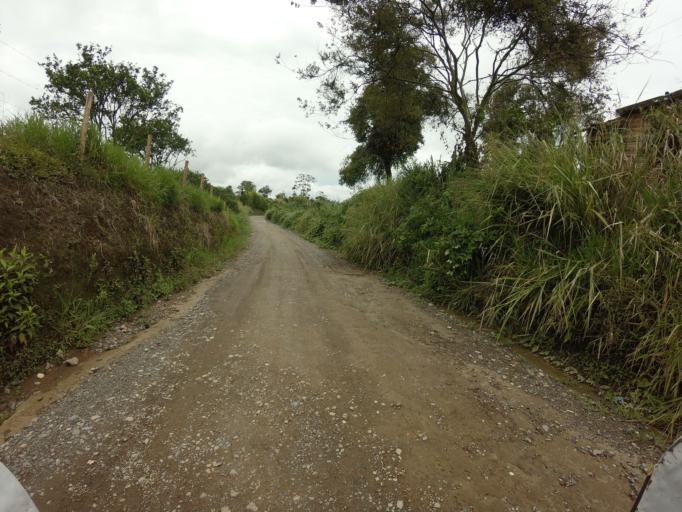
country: CO
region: Valle del Cauca
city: Ulloa
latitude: 4.6974
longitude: -75.7299
